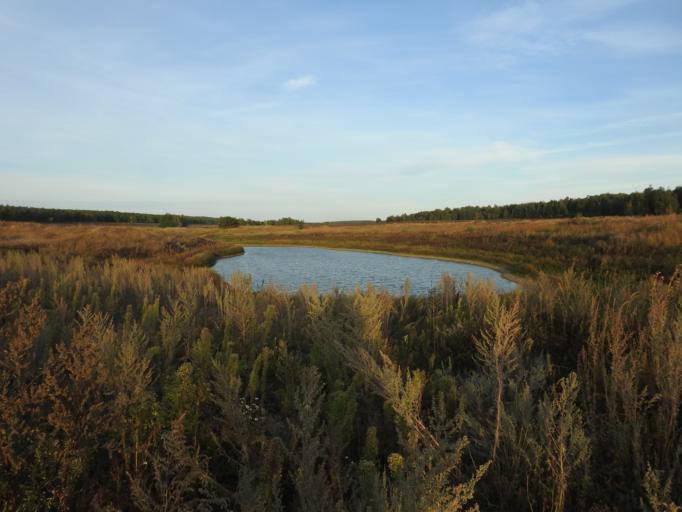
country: RU
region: Saratov
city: Novyye Burasy
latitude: 52.1920
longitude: 46.1029
